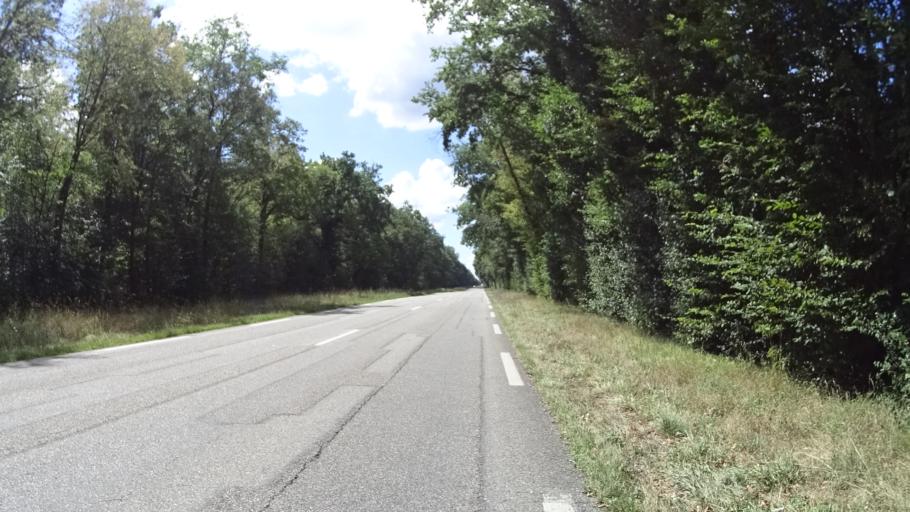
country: FR
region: Alsace
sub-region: Departement du Haut-Rhin
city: Ottmarsheim
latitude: 47.7788
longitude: 7.4867
